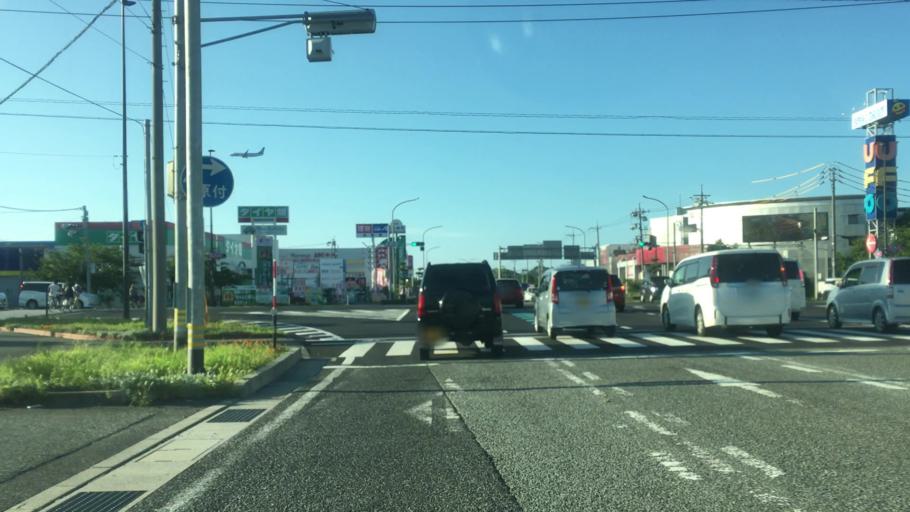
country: JP
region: Tottori
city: Tottori
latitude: 35.5190
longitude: 134.2023
